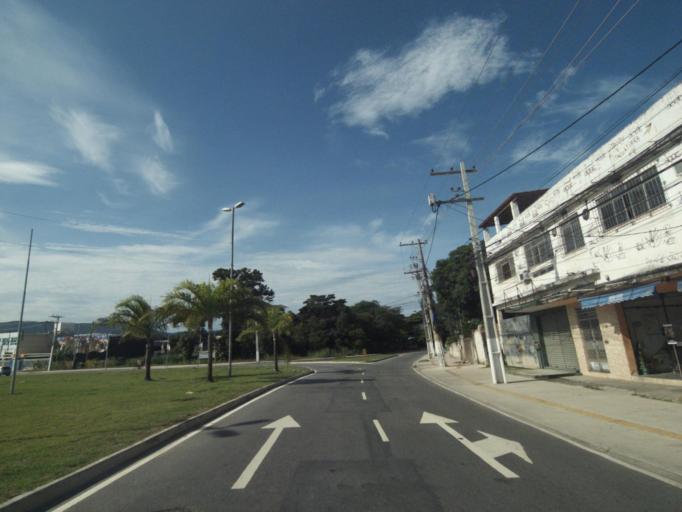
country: BR
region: Rio de Janeiro
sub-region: Niteroi
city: Niteroi
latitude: -22.9536
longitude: -43.0278
